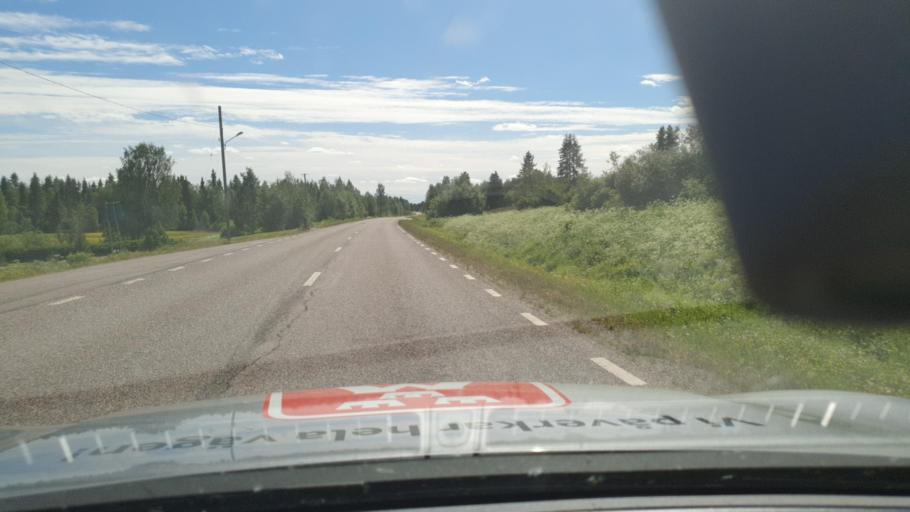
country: FI
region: Lapland
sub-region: Torniolaakso
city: Pello
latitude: 66.9421
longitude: 23.8513
